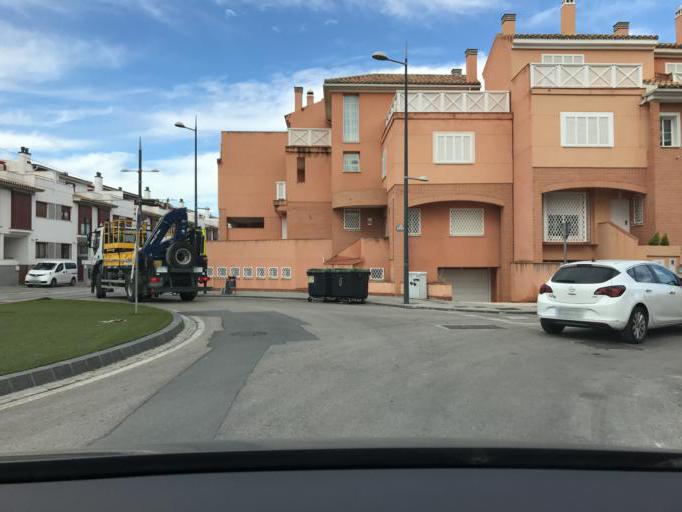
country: ES
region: Andalusia
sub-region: Provincia de Granada
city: Armilla
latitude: 37.1454
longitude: -3.6165
